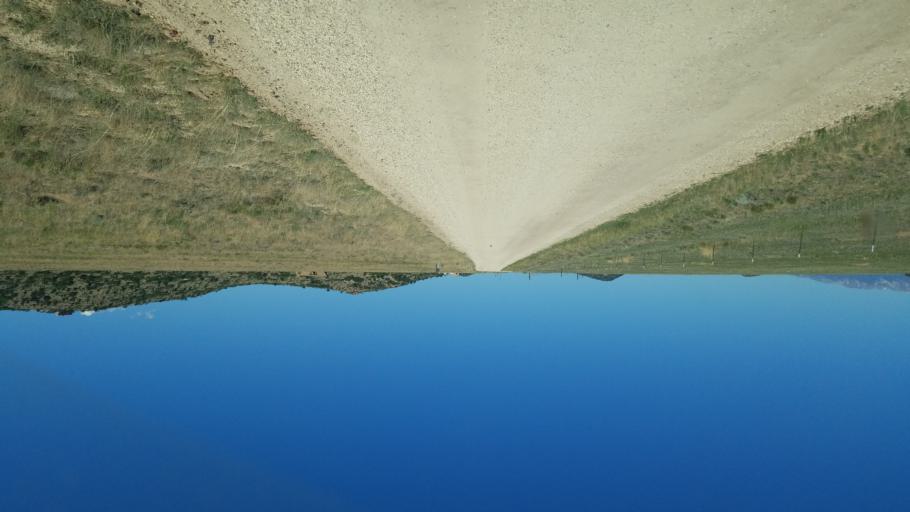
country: US
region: Colorado
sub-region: Custer County
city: Westcliffe
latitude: 38.2370
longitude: -105.4896
